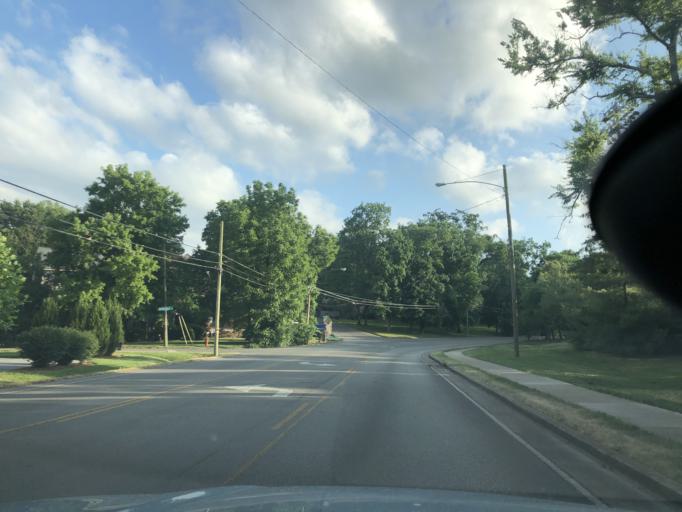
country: US
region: Tennessee
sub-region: Davidson County
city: Oak Hill
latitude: 36.1028
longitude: -86.7977
